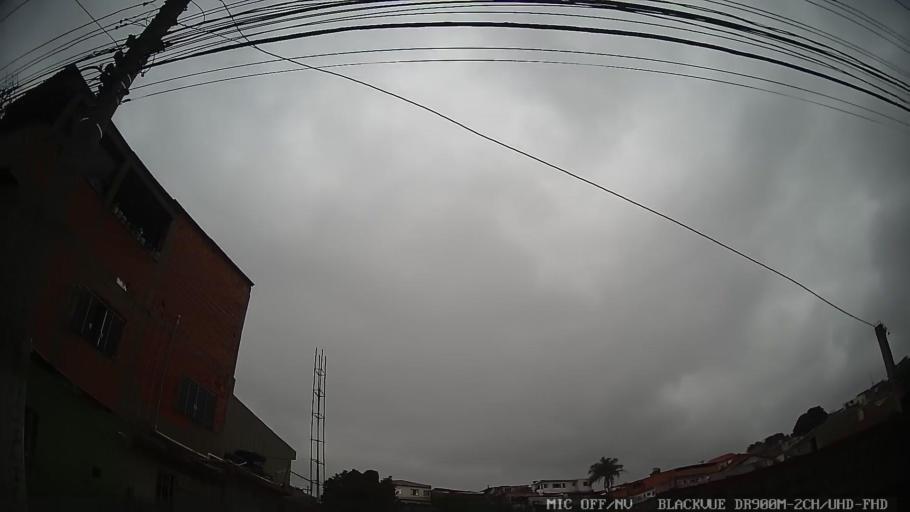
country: BR
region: Sao Paulo
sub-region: Osasco
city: Osasco
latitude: -23.4542
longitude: -46.7506
